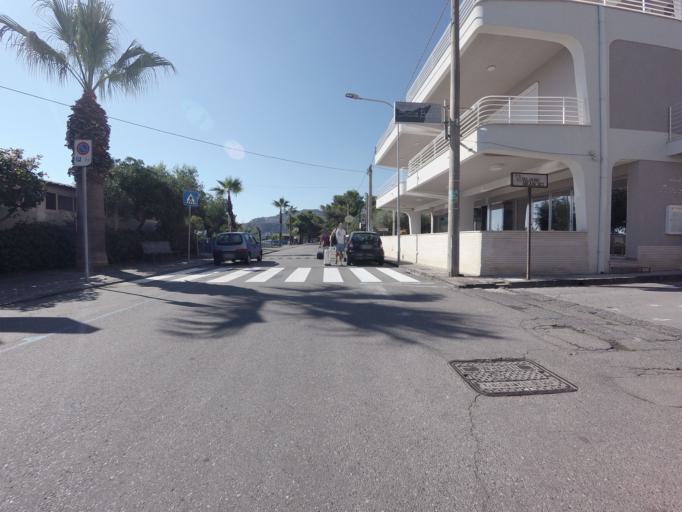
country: IT
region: Sicily
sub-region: Messina
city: Letojanni
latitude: 37.8734
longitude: 15.3019
